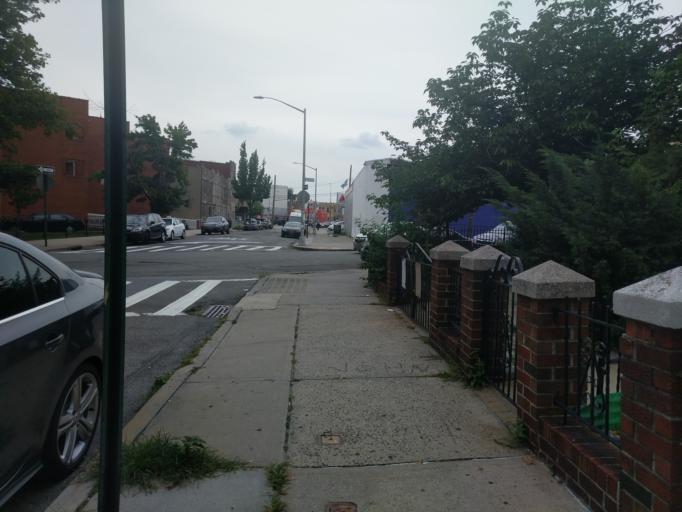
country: US
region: New York
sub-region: Queens County
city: Long Island City
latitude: 40.7593
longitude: -73.9142
